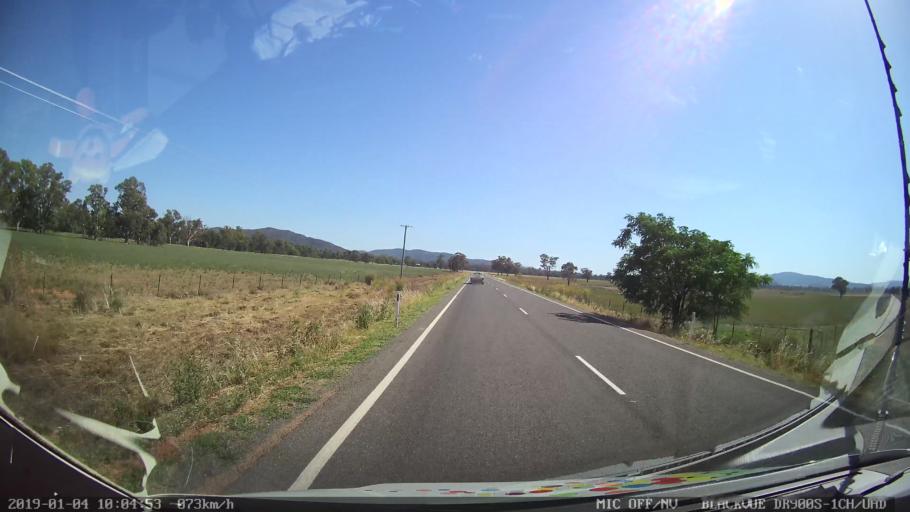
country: AU
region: New South Wales
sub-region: Cabonne
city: Canowindra
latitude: -33.4480
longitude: 148.3629
